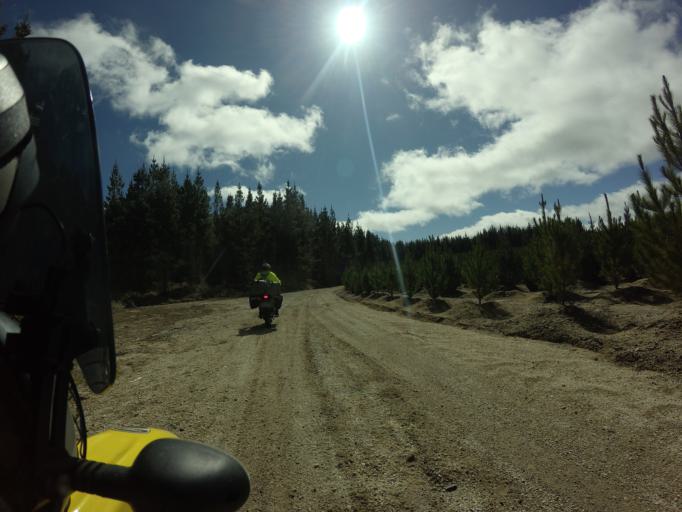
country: NZ
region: Bay of Plenty
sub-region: Whakatane District
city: Murupara
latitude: -38.8220
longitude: 176.5499
